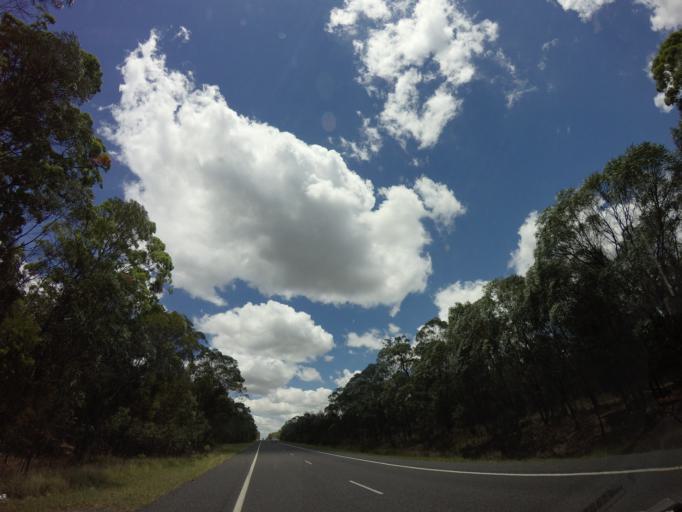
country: AU
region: Queensland
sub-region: Western Downs
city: Dalby
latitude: -27.9716
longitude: 151.0446
